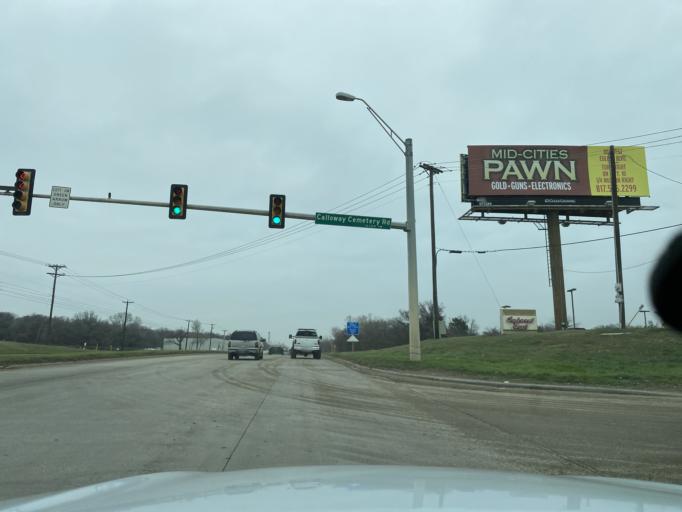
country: US
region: Texas
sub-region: Tarrant County
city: Euless
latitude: 32.8109
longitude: -97.0996
